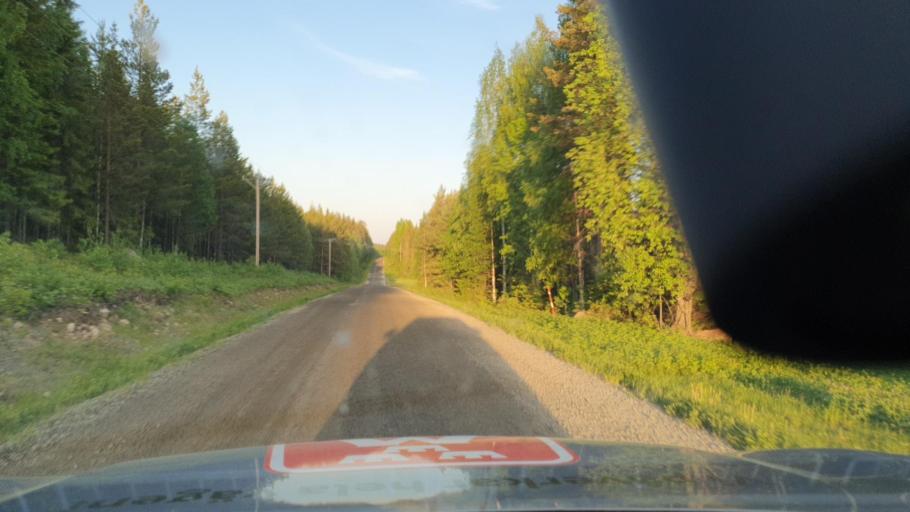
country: SE
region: Norrbotten
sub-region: Bodens Kommun
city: Boden
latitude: 66.0676
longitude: 21.7163
